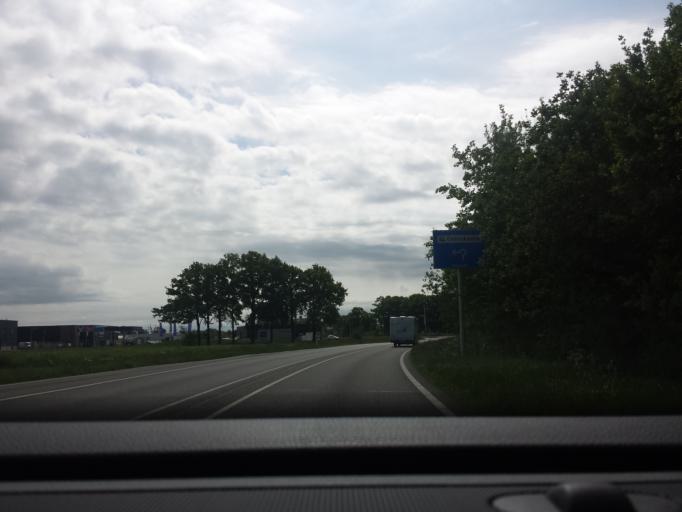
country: NL
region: Gelderland
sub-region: Gemeente Lochem
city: Barchem
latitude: 52.0777
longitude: 6.4553
